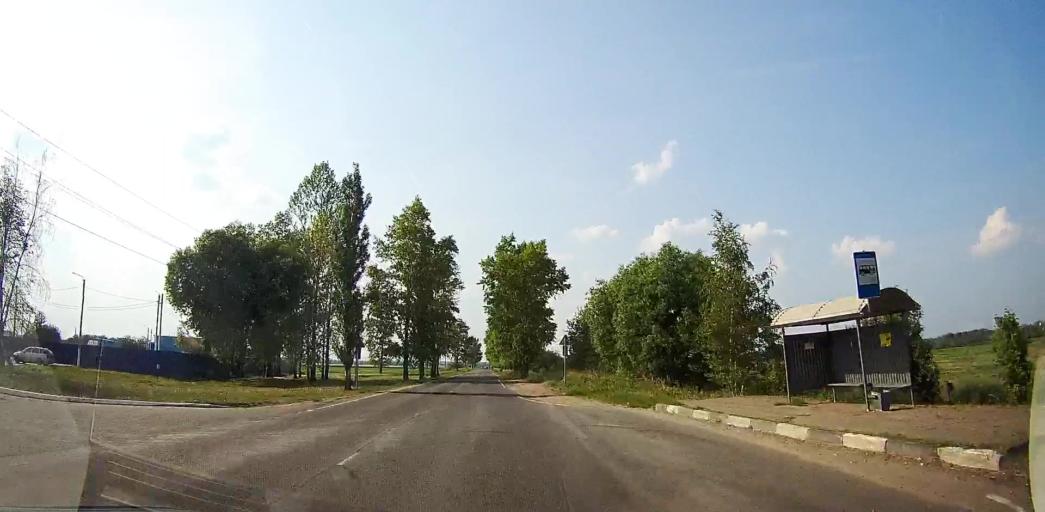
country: RU
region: Moskovskaya
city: Yakovlevskoye
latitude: 55.4742
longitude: 37.9652
